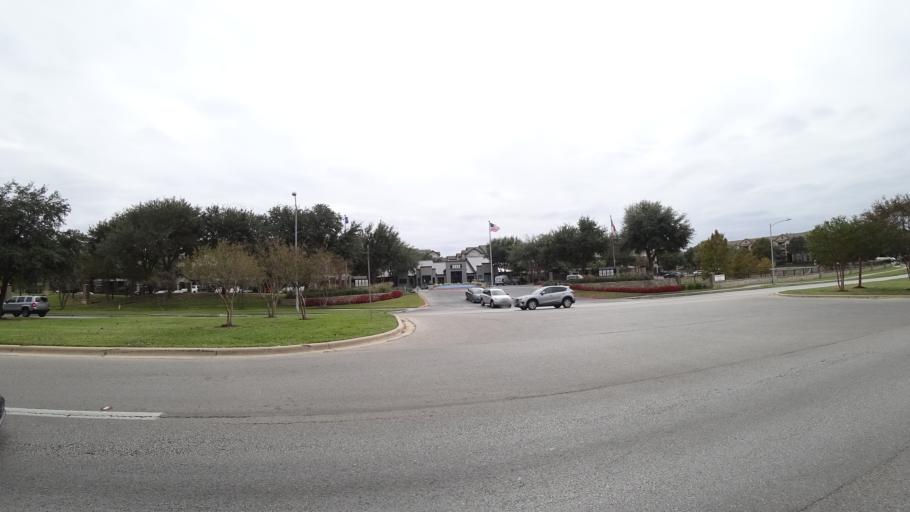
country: US
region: Texas
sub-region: Travis County
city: Wells Branch
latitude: 30.4418
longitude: -97.6905
